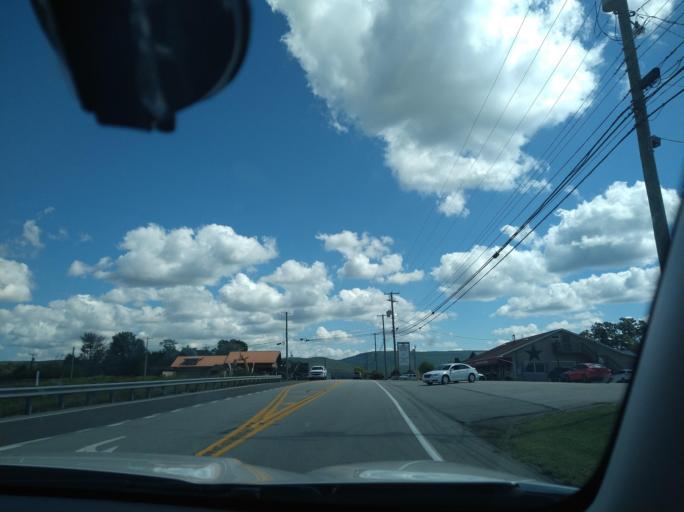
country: US
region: Pennsylvania
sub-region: Fayette County
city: Bear Rocks
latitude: 40.0998
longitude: -79.3622
